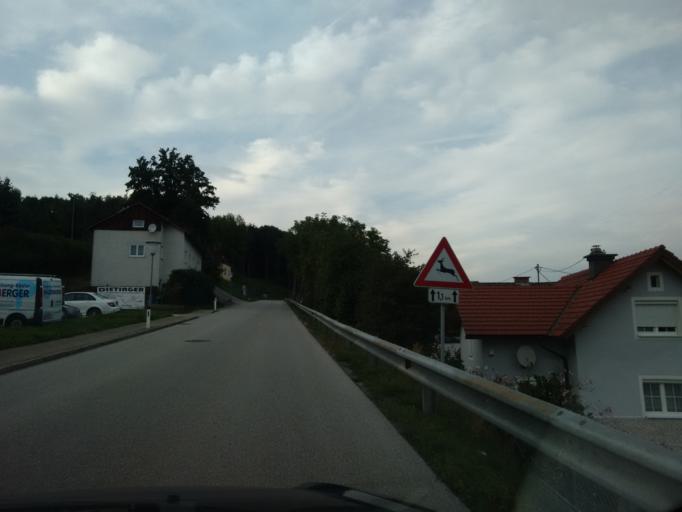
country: AT
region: Upper Austria
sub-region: Politischer Bezirk Steyr-Land
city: Pfarrkirchen bei Bad Hall
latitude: 48.0391
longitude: 14.1979
